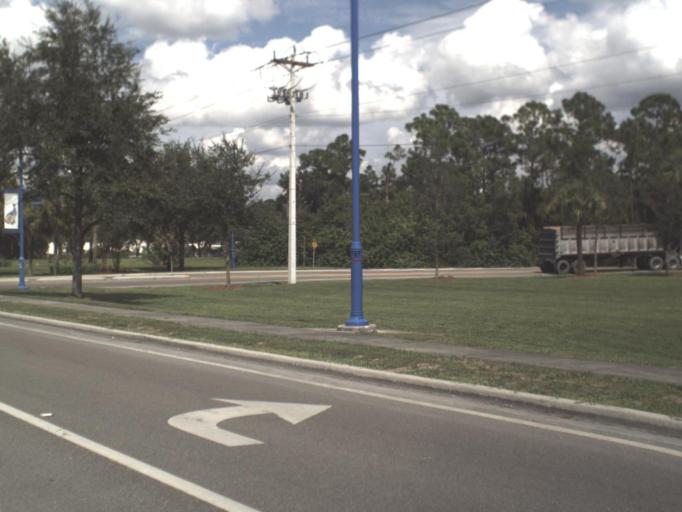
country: US
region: Florida
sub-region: Collier County
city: Immokalee
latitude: 26.4409
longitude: -81.4339
